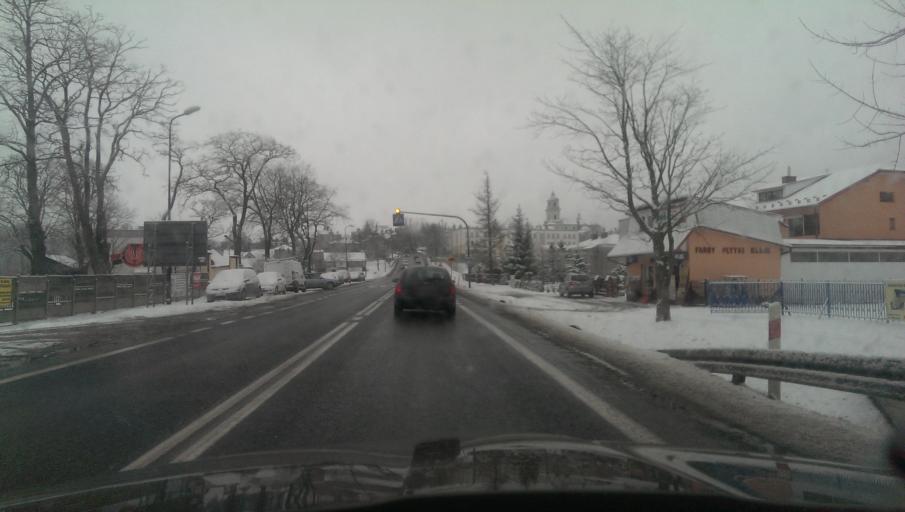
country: PL
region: Subcarpathian Voivodeship
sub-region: Powiat krosnienski
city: Rymanow
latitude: 49.5786
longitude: 21.8604
